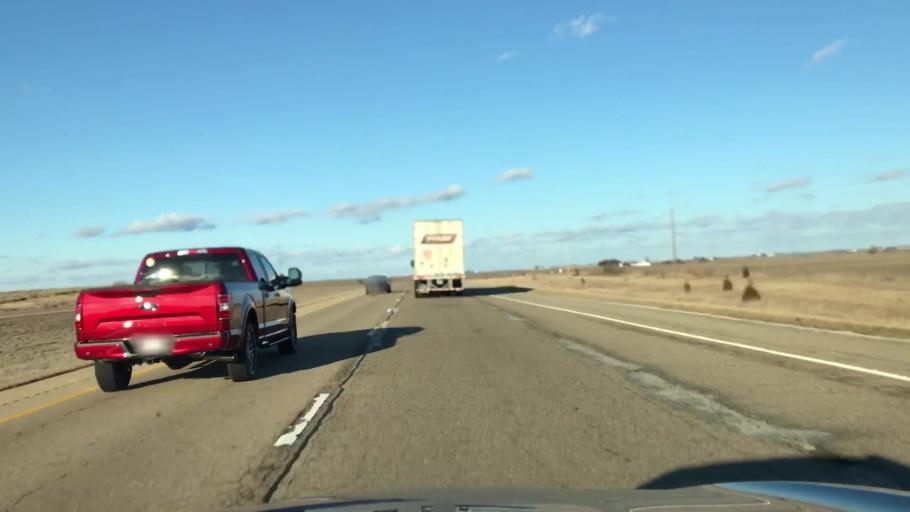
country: US
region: Illinois
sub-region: McLean County
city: Lexington
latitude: 40.6497
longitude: -88.8066
